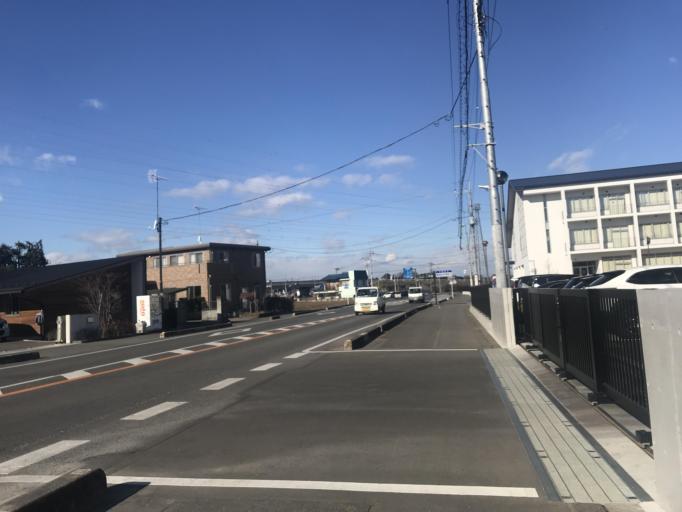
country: JP
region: Tochigi
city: Kaminokawa
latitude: 36.3865
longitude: 139.8750
